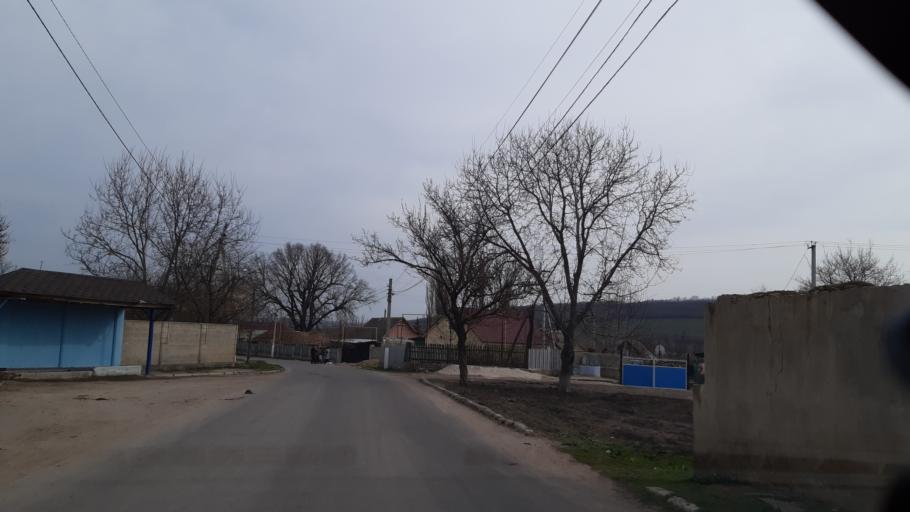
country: MD
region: Soldanesti
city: Soldanesti
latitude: 47.6843
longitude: 28.7794
